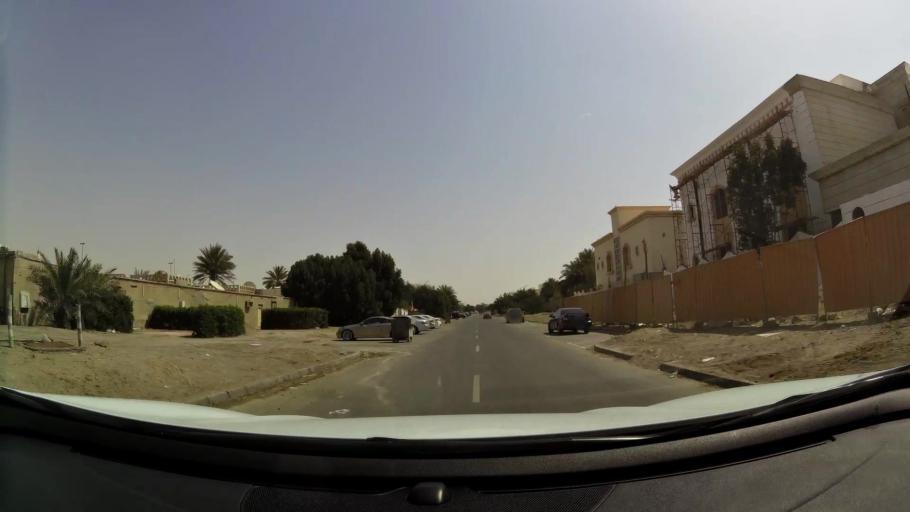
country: AE
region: Abu Dhabi
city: Abu Dhabi
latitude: 24.2927
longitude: 54.6439
